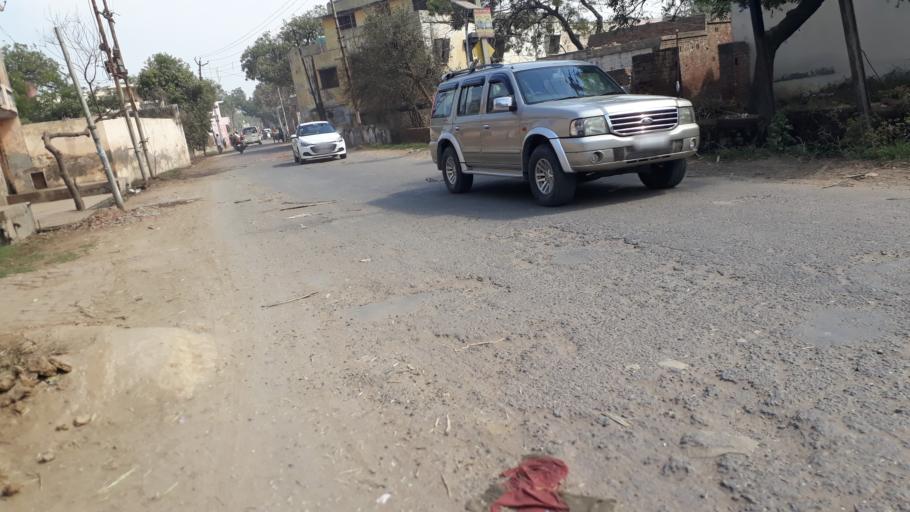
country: IN
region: Uttar Pradesh
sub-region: Baghpat
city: Baraut
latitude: 29.0949
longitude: 77.3999
